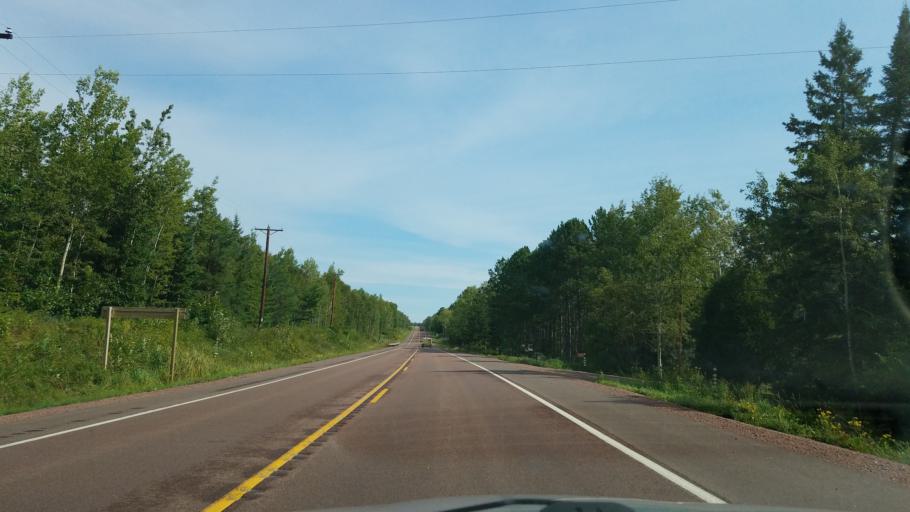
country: US
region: Wisconsin
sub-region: Ashland County
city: Ashland
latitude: 46.6078
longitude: -90.9465
